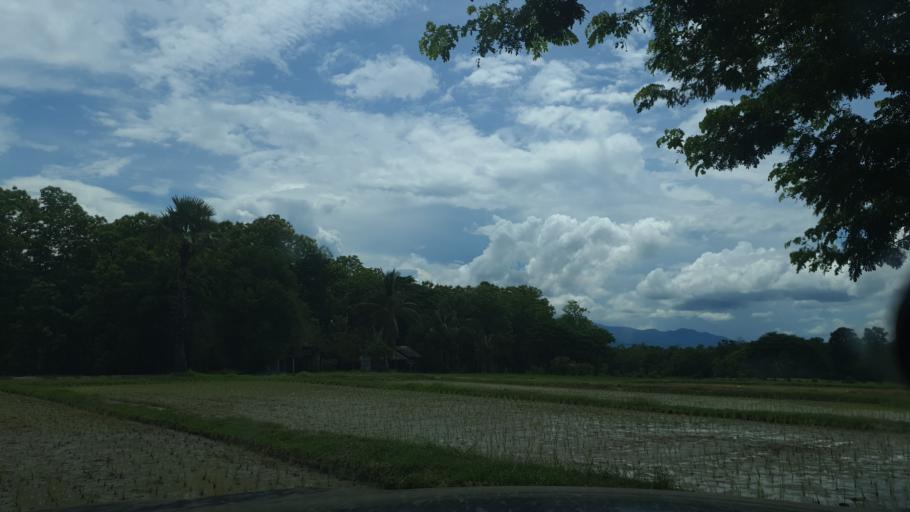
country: TH
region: Lampang
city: Sop Prap
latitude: 17.8540
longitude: 99.3975
